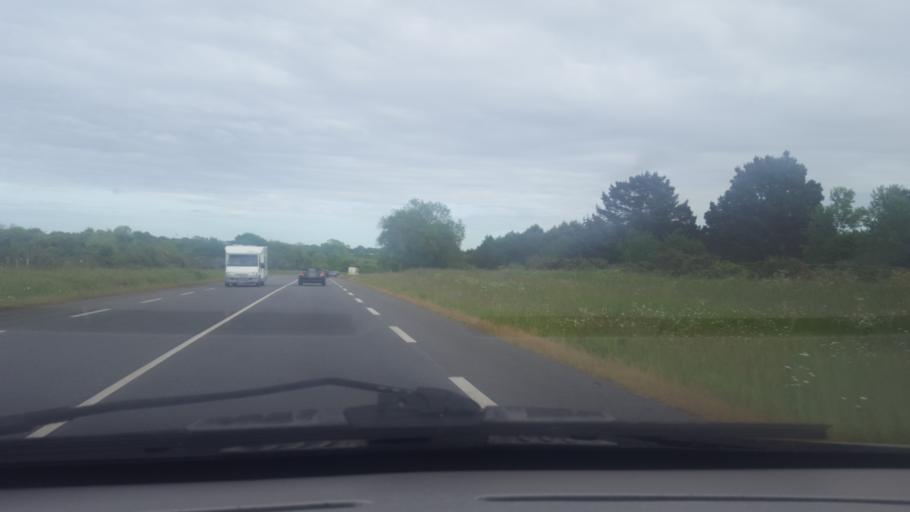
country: FR
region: Pays de la Loire
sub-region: Departement de la Loire-Atlantique
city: Les Moutiers-en-Retz
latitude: 47.0762
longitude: -2.0051
